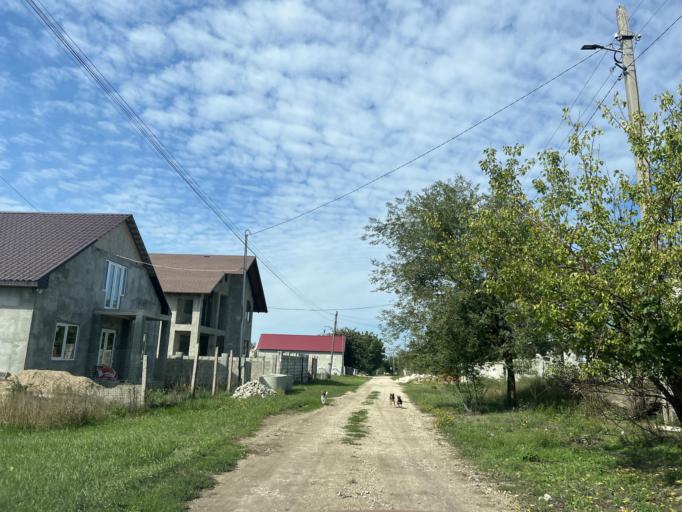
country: MD
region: Ungheni
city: Ungheni
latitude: 47.2018
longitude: 27.8168
